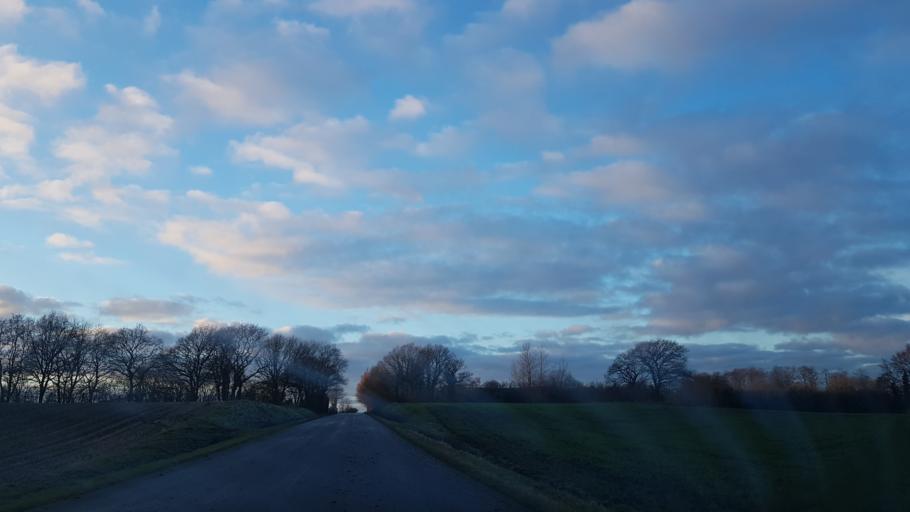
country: DK
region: South Denmark
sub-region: Kolding Kommune
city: Vamdrup
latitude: 55.3665
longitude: 9.3188
